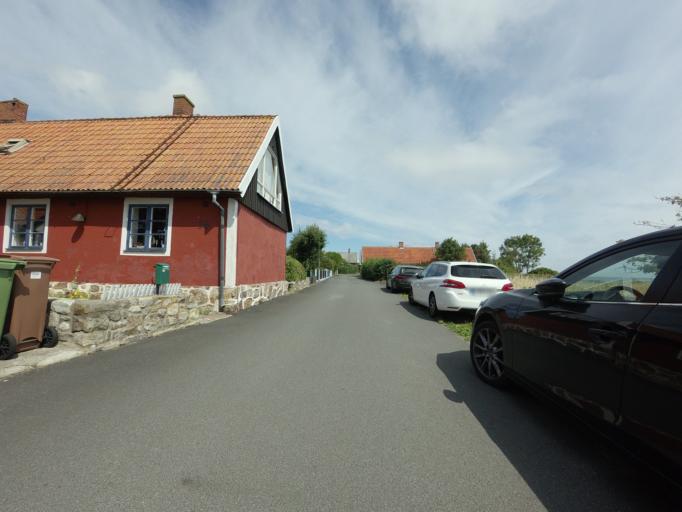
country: SE
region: Skane
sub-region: Simrishamns Kommun
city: Simrishamn
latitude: 55.5187
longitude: 14.3464
